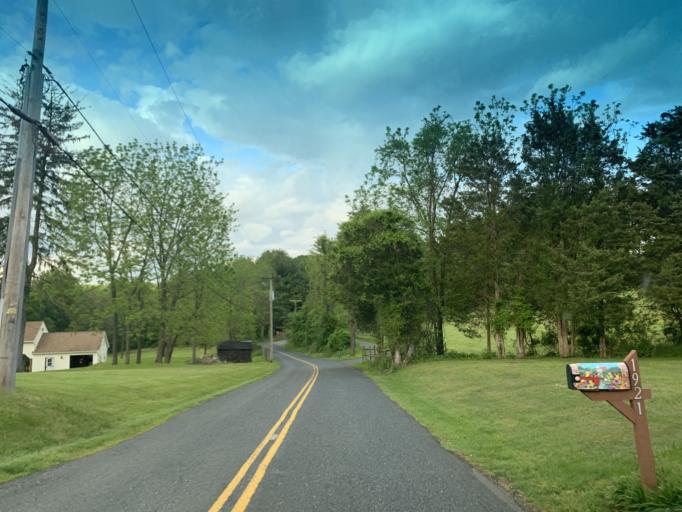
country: US
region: Pennsylvania
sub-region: York County
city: Susquehanna Trails
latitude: 39.6973
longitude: -76.2728
